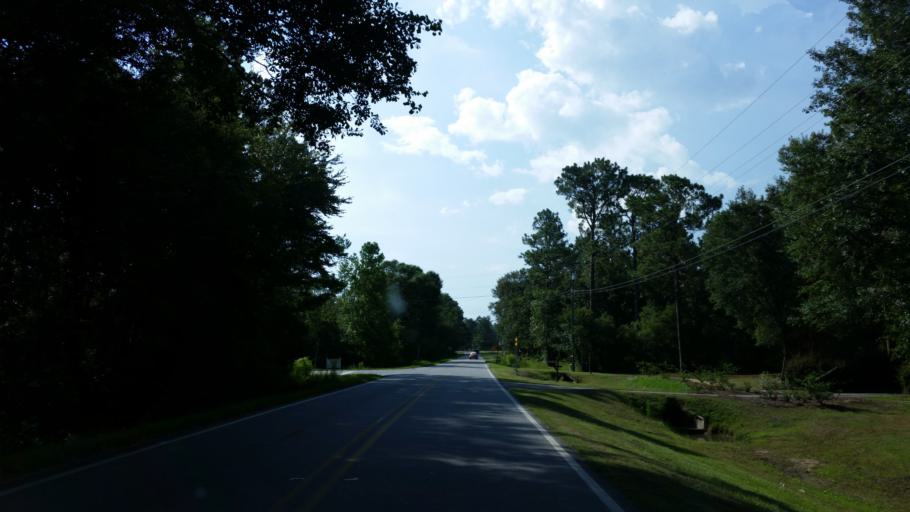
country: US
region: Georgia
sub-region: Lowndes County
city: Remerton
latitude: 30.8949
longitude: -83.3701
